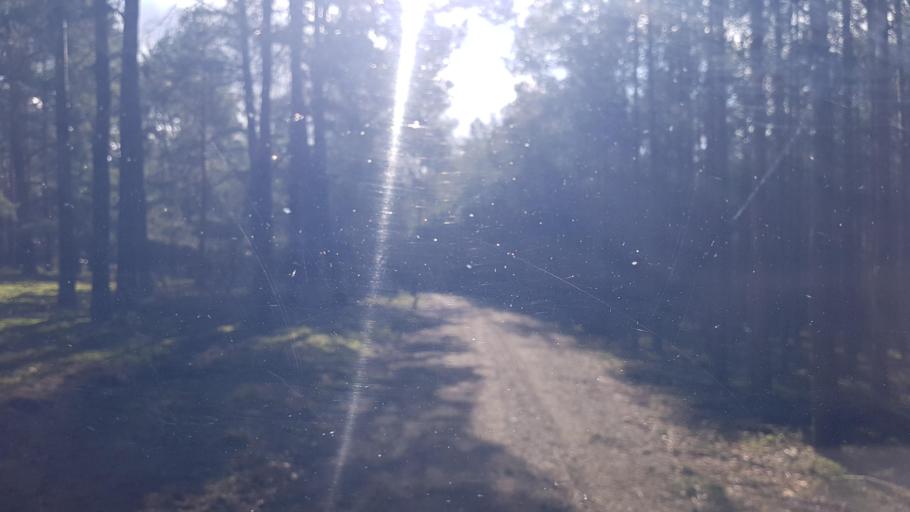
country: DE
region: Brandenburg
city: Schlieben
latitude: 51.6846
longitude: 13.4014
